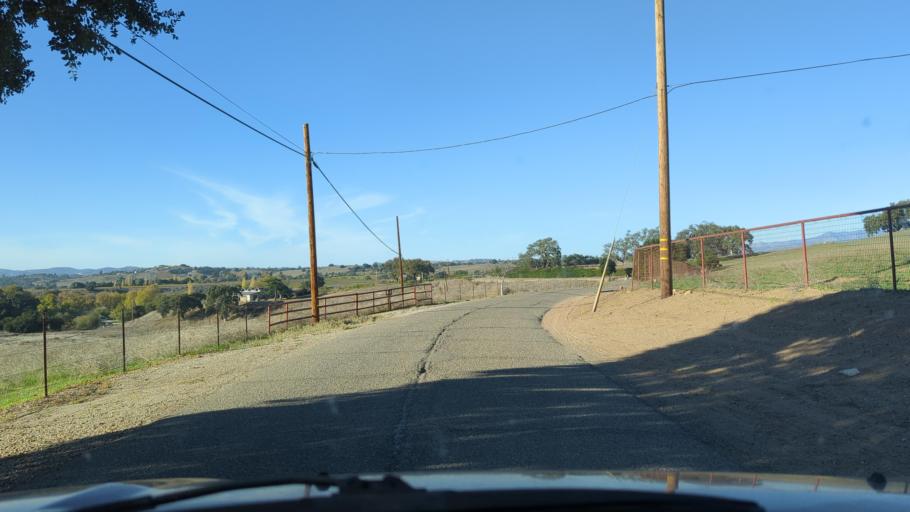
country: US
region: California
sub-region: Santa Barbara County
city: Santa Ynez
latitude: 34.5765
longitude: -120.0988
